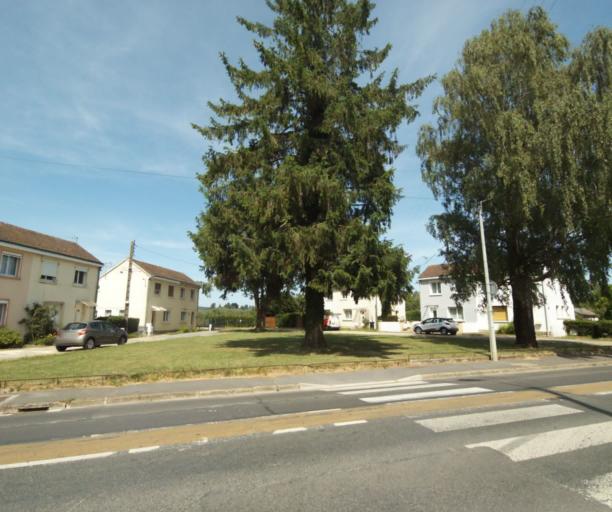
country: FR
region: Champagne-Ardenne
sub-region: Departement des Ardennes
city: Warcq
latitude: 49.7666
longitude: 4.6876
